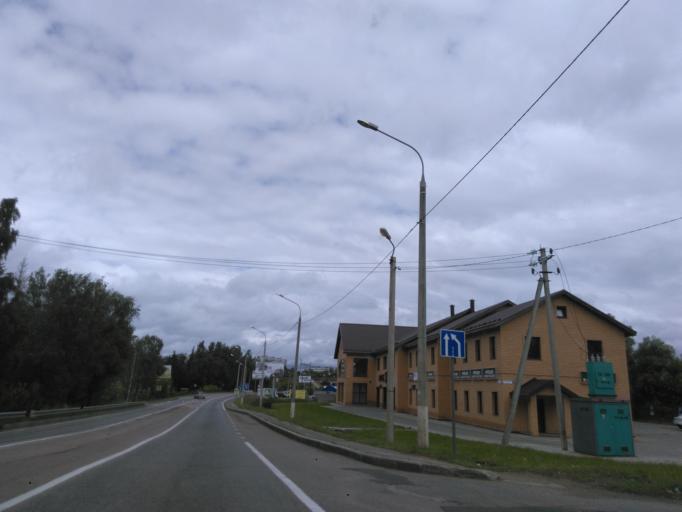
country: RU
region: Moskovskaya
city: Solnechnogorsk
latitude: 56.1852
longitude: 36.9617
